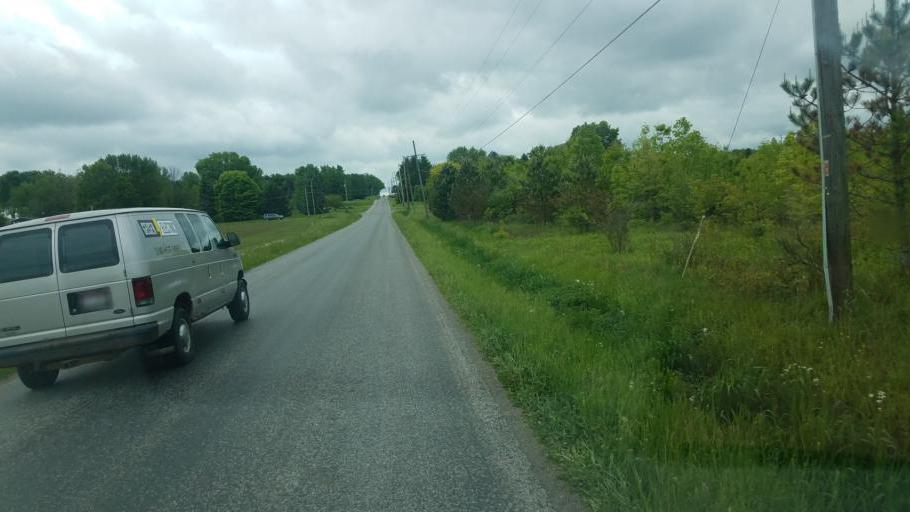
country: US
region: Ohio
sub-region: Wayne County
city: Orrville
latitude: 40.7843
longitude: -81.7552
